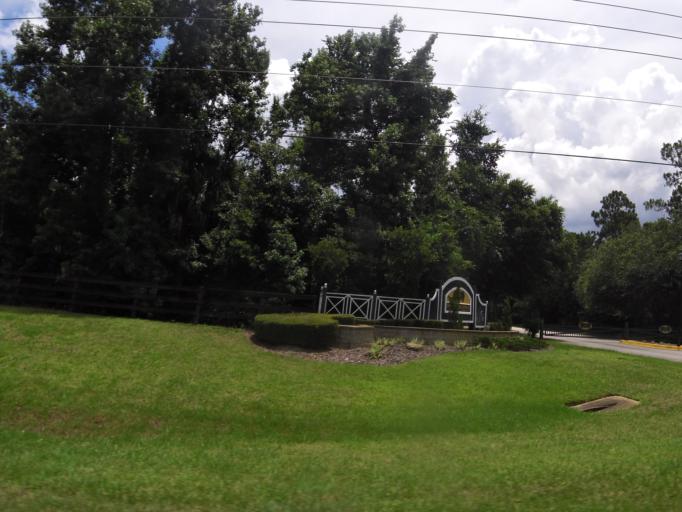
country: US
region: Florida
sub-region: Flagler County
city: Palm Coast
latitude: 29.6585
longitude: -81.2930
